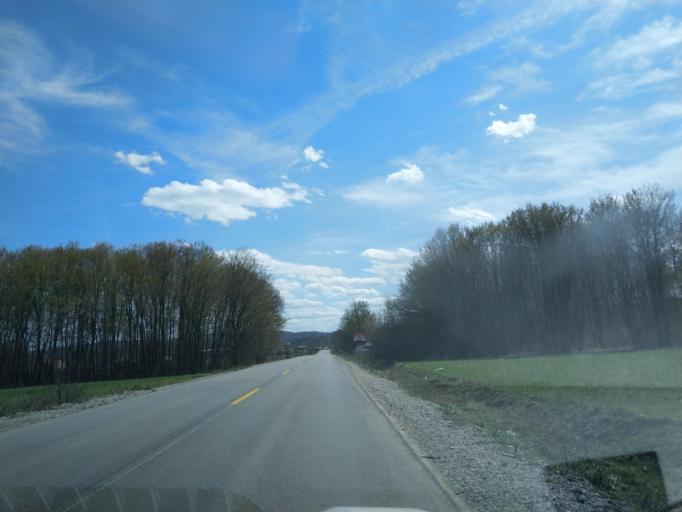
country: RS
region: Central Serbia
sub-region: Zlatiborski Okrug
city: Arilje
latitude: 43.8068
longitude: 20.0925
